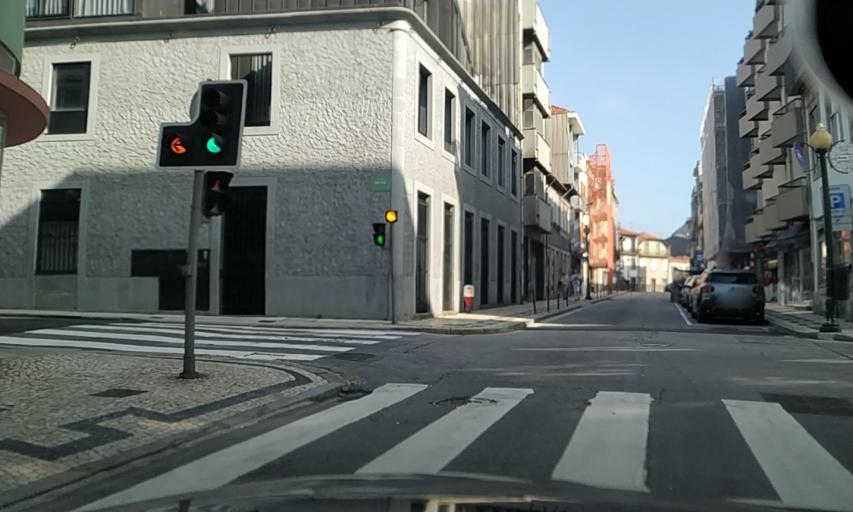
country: PT
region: Porto
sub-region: Porto
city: Porto
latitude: 41.1506
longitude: -8.6210
